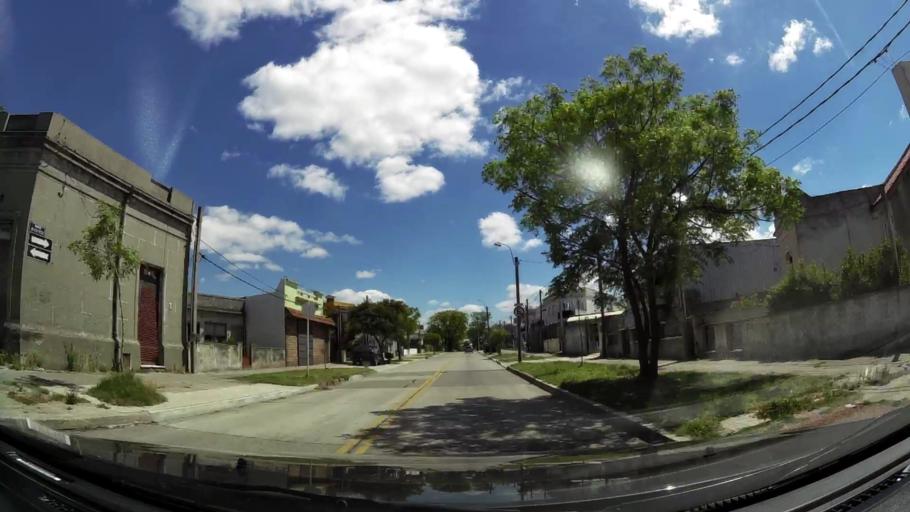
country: UY
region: Montevideo
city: Montevideo
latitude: -34.8586
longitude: -56.1348
